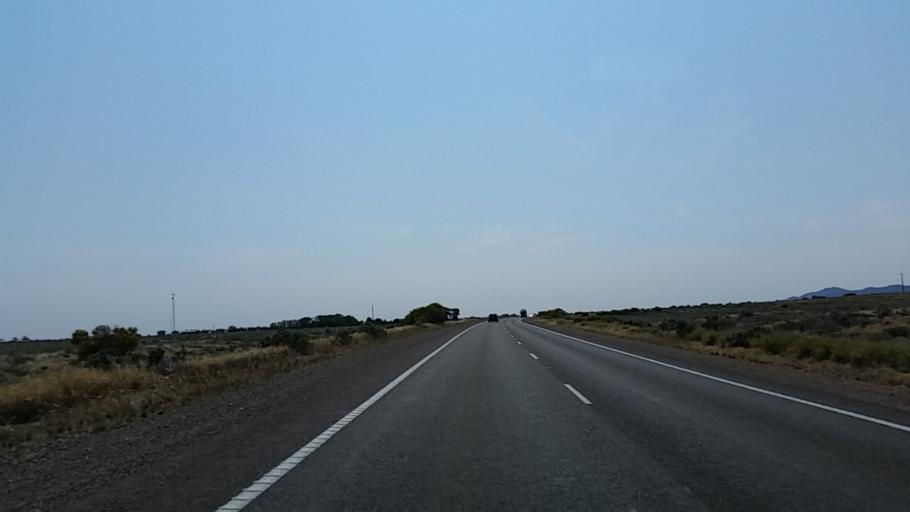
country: AU
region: South Australia
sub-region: Port Augusta
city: Port Augusta
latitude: -32.7394
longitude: 137.9420
